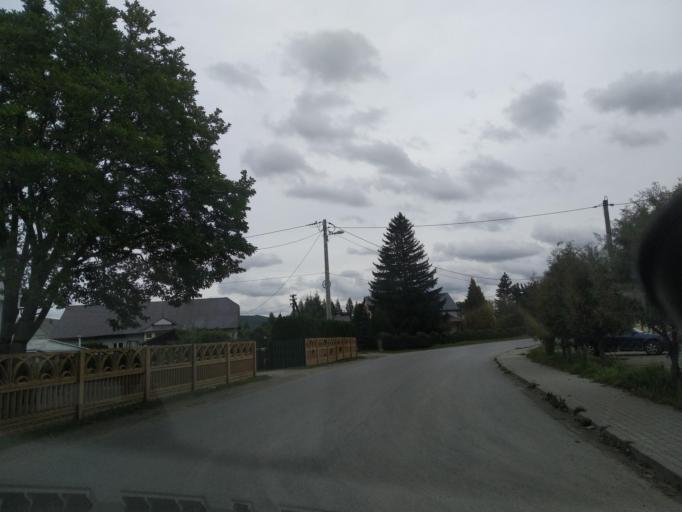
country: PL
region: Subcarpathian Voivodeship
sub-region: Powiat krosnienski
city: Dukla
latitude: 49.5542
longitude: 21.6887
